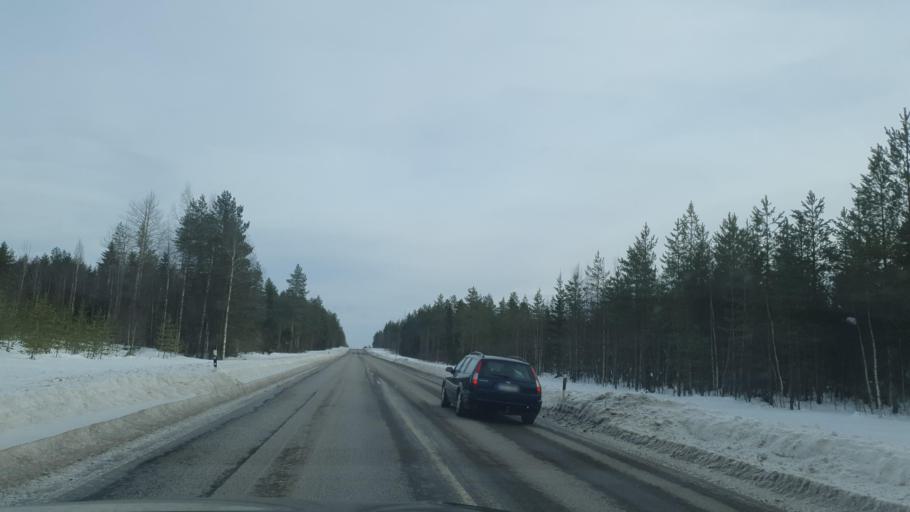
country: FI
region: Kainuu
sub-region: Kajaani
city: Vaala
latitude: 64.5519
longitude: 27.0582
